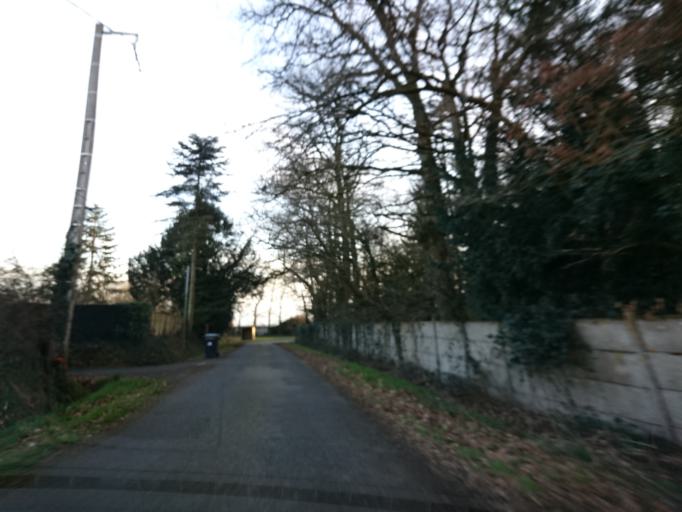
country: FR
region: Brittany
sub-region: Departement d'Ille-et-Vilaine
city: Chanteloup
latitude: 47.9144
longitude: -1.6082
